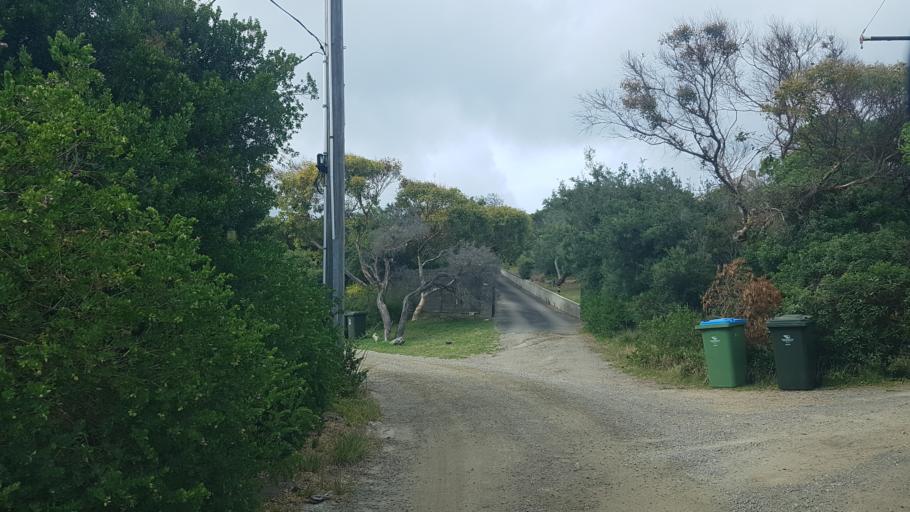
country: AU
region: Victoria
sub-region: Mornington Peninsula
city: Sorrento
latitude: -38.3296
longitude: 144.7041
